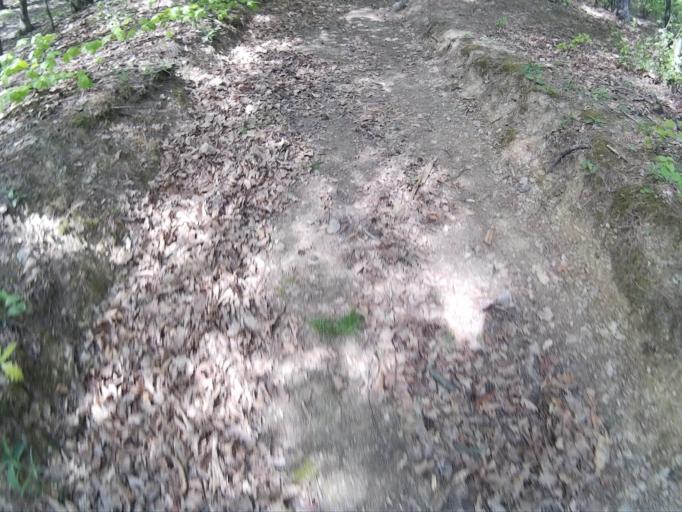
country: HU
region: Vas
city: Koszeg
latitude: 47.3560
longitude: 16.5048
